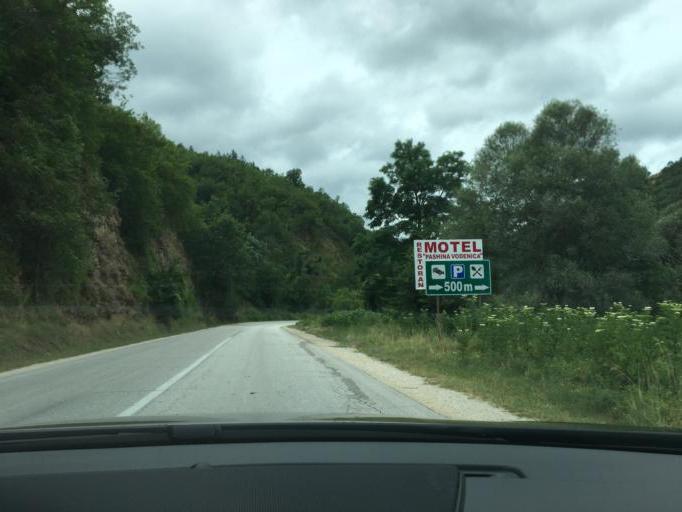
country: MK
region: Kriva Palanka
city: Kriva Palanka
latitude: 42.2289
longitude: 22.3610
